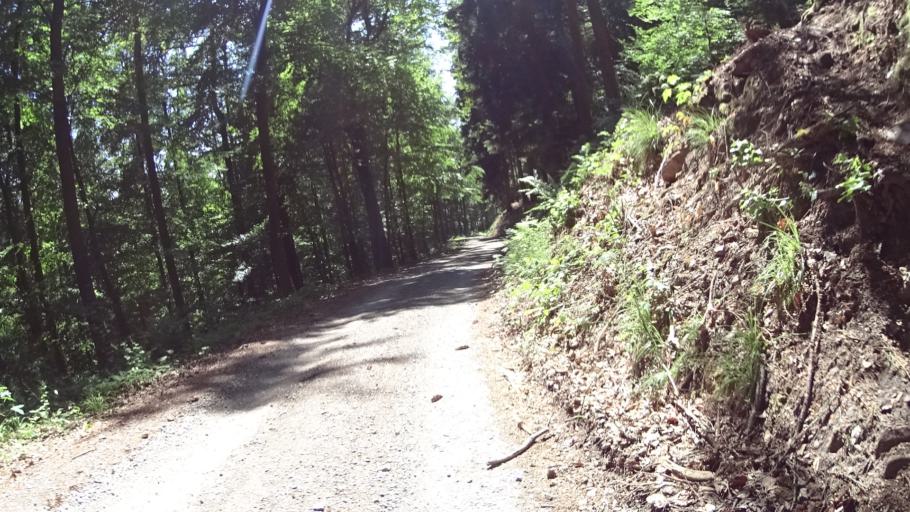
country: DE
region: Baden-Wuerttemberg
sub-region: Karlsruhe Region
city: Neckargemund
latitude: 49.4034
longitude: 8.7986
